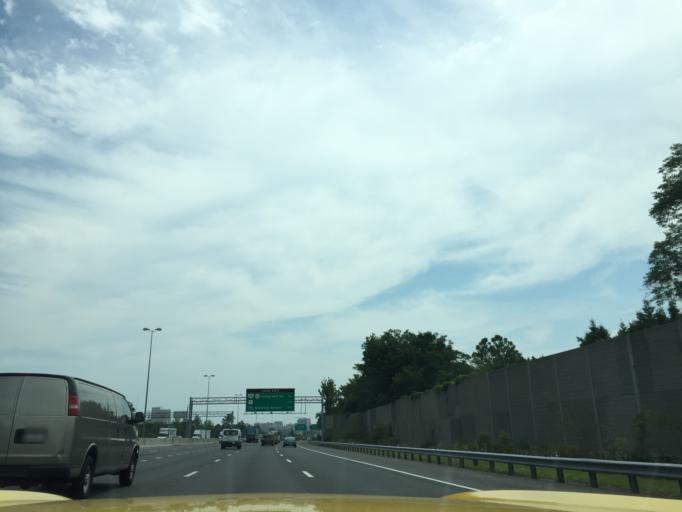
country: US
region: Virginia
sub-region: Fairfax County
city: Rose Hill
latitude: 38.8030
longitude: -77.1030
